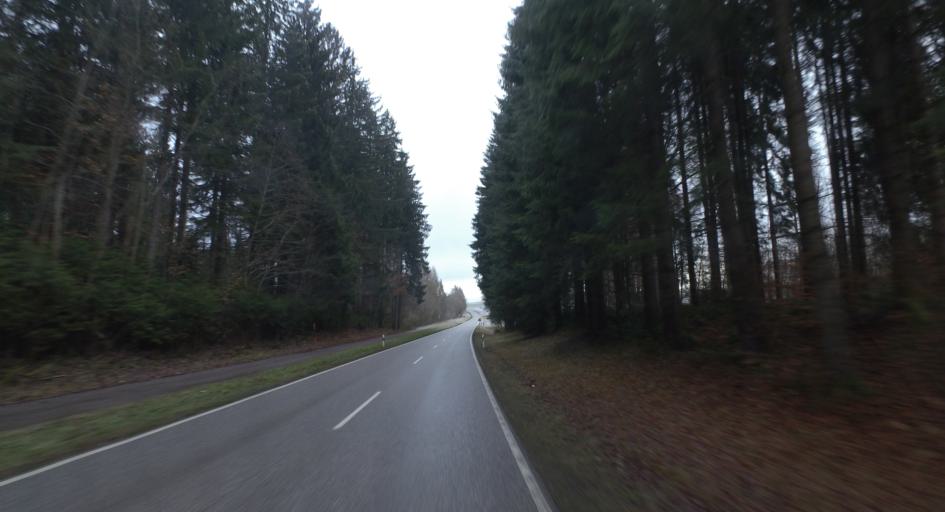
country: DE
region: Bavaria
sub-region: Upper Bavaria
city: Traunstein
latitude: 47.9008
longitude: 12.6449
